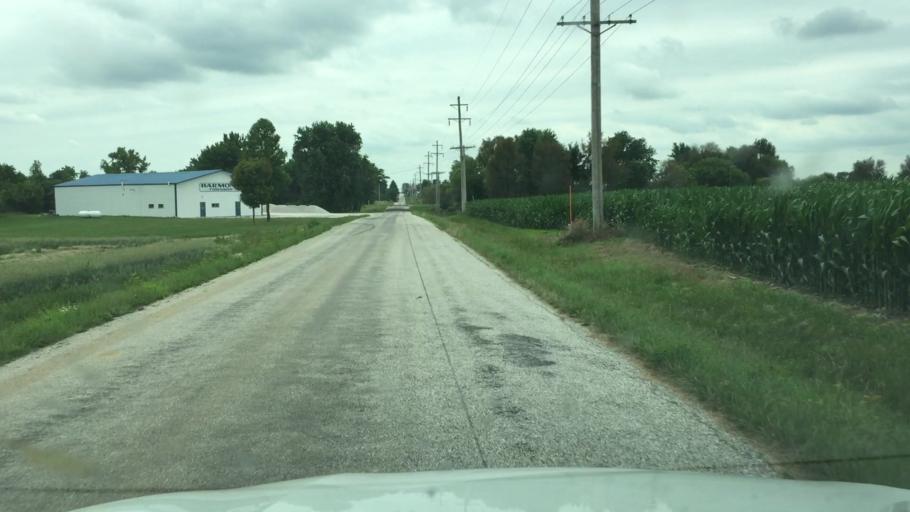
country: US
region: Illinois
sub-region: Hancock County
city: Carthage
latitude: 40.3330
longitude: -91.0825
